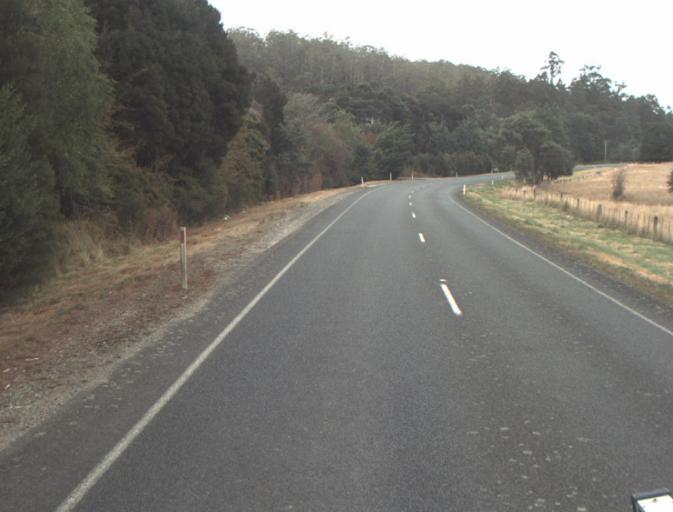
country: AU
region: Tasmania
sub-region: Launceston
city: Mayfield
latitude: -41.2777
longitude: 147.2200
